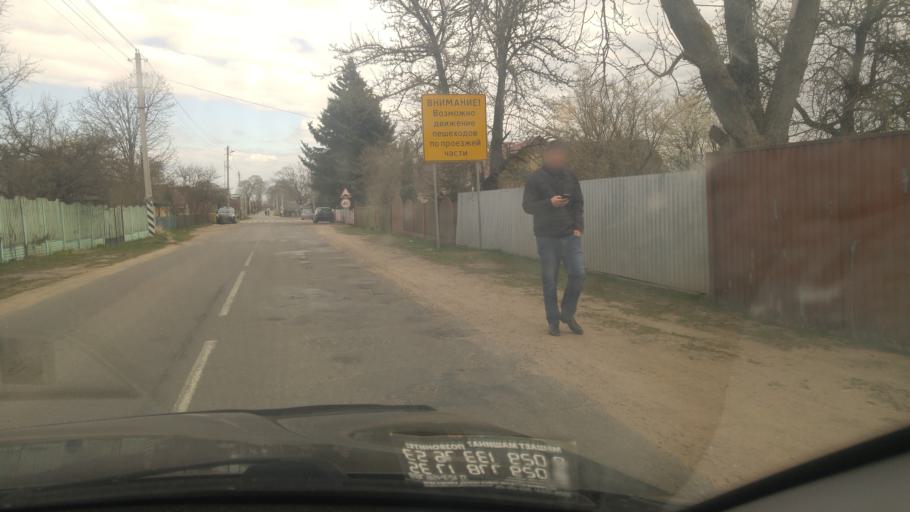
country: BY
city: Michanovichi
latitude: 53.6633
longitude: 27.7661
